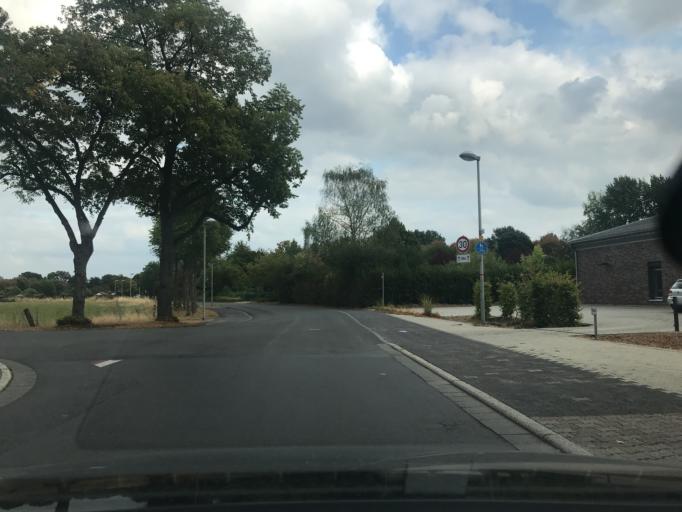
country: DE
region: North Rhine-Westphalia
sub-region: Regierungsbezirk Dusseldorf
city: Krefeld
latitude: 51.3654
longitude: 6.6007
